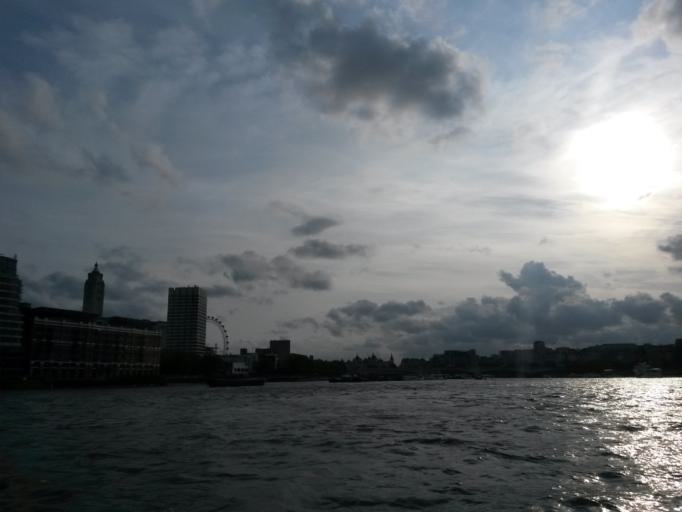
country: GB
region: England
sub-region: Greater London
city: City of London
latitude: 51.5104
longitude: -0.1055
